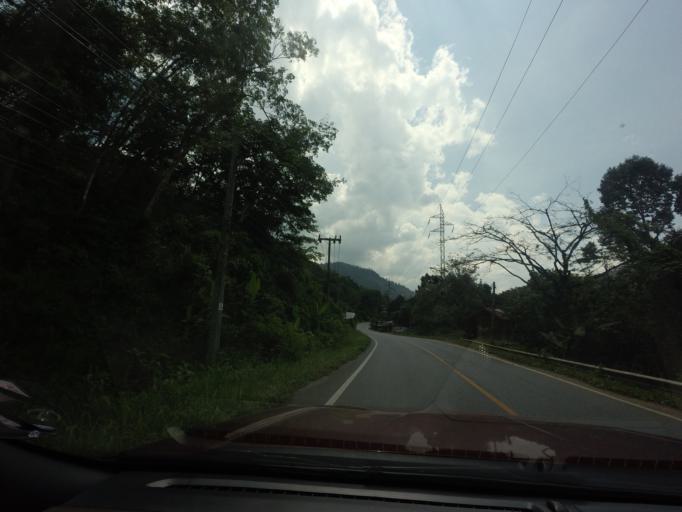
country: TH
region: Yala
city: Than To
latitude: 5.9854
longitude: 101.1943
